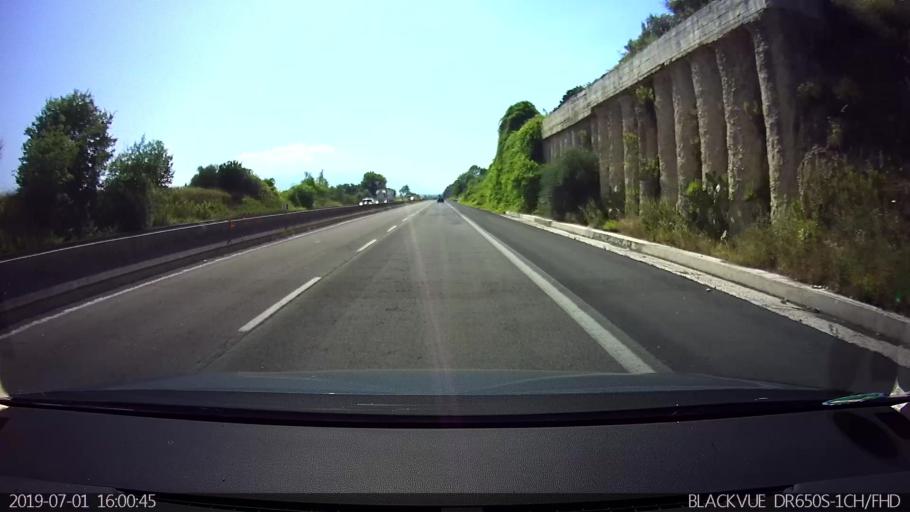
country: IT
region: Latium
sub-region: Provincia di Frosinone
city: Castelmassimo
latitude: 41.6643
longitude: 13.3893
